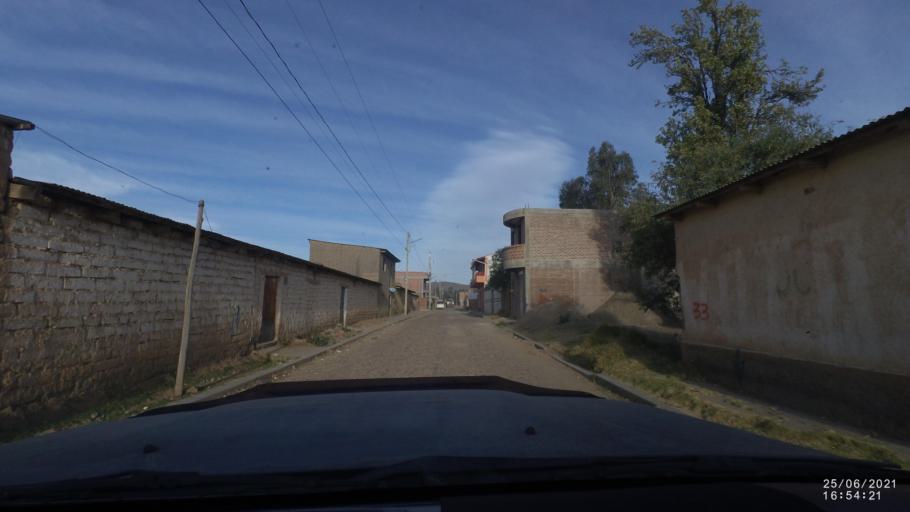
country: BO
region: Cochabamba
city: Arani
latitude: -17.8180
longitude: -65.7767
